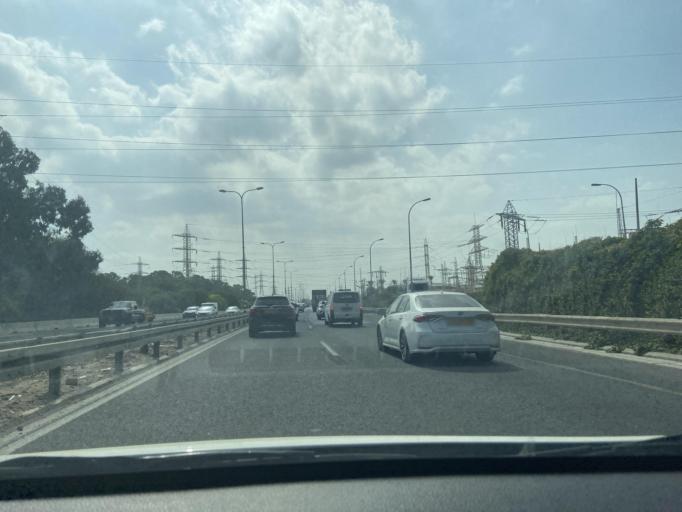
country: IL
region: Northern District
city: `Akko
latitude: 32.8967
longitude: 35.0934
